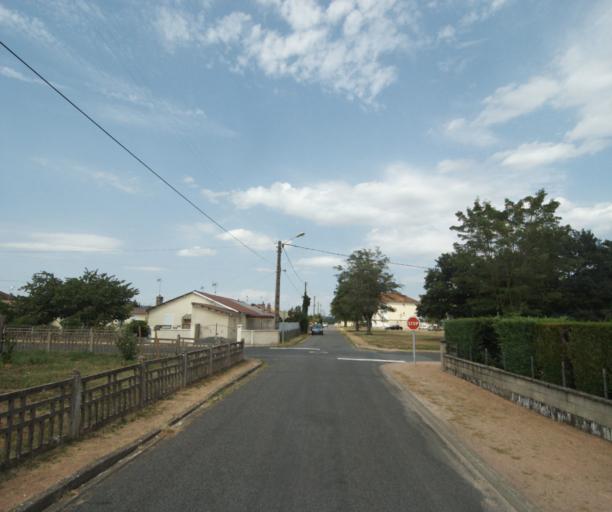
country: FR
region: Bourgogne
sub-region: Departement de Saone-et-Loire
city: Gueugnon
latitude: 46.6063
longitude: 4.0535
